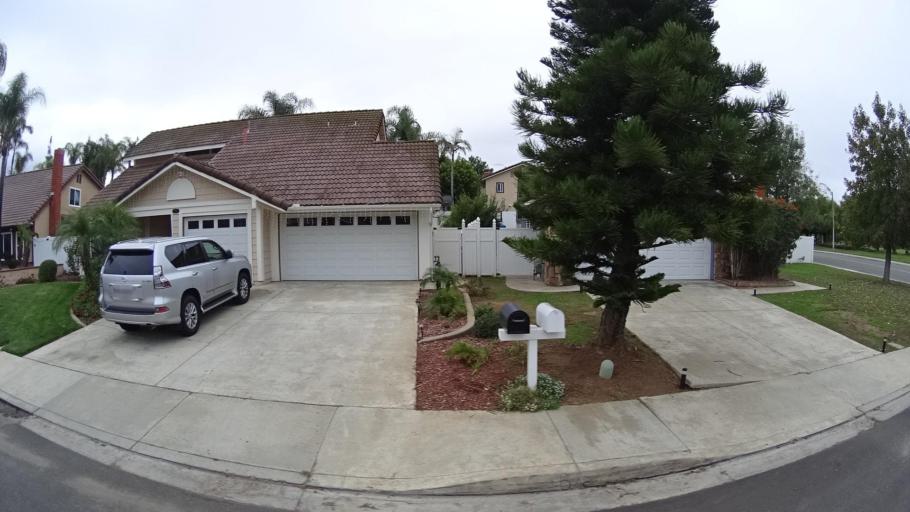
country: US
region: California
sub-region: San Diego County
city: Rancho San Diego
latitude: 32.7592
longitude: -116.9101
